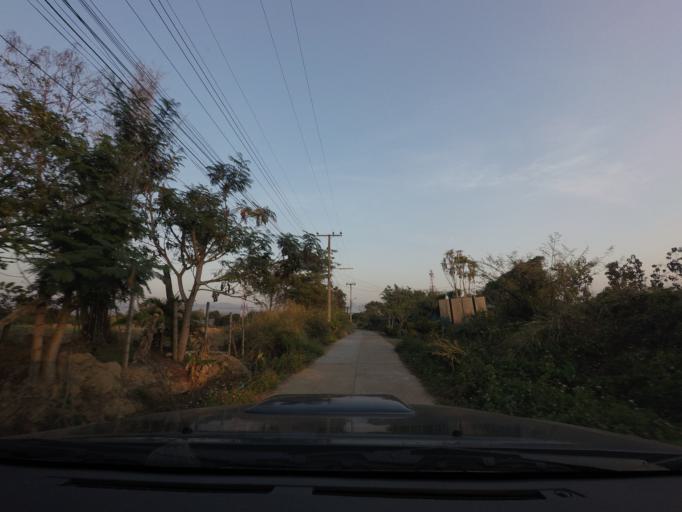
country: TH
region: Chiang Mai
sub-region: Amphoe Chiang Dao
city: Chiang Dao
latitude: 19.3680
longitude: 98.9594
